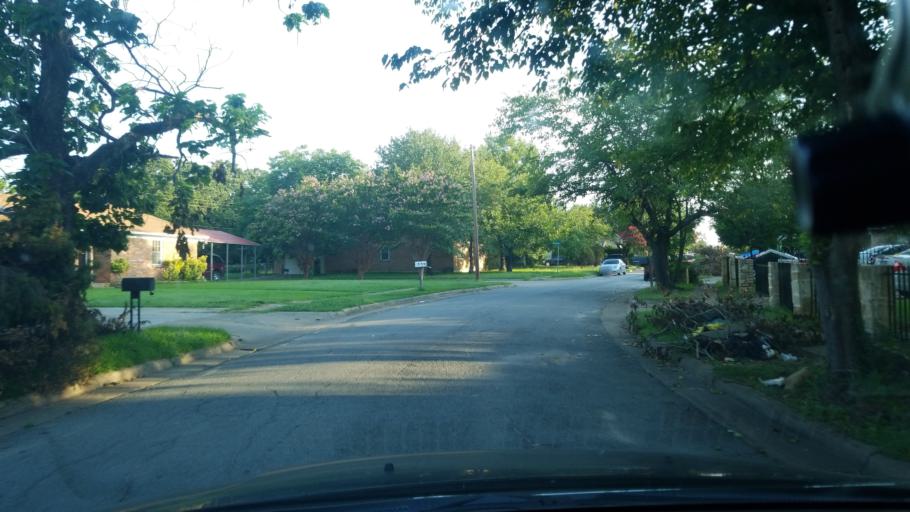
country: US
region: Texas
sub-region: Dallas County
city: Balch Springs
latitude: 32.7212
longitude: -96.6607
